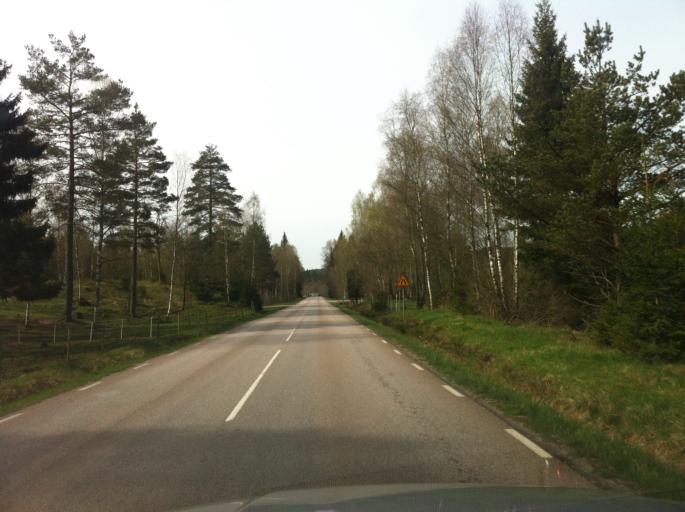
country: SE
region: Vaestra Goetaland
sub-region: Bollebygds Kommun
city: Bollebygd
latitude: 57.7267
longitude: 12.5892
